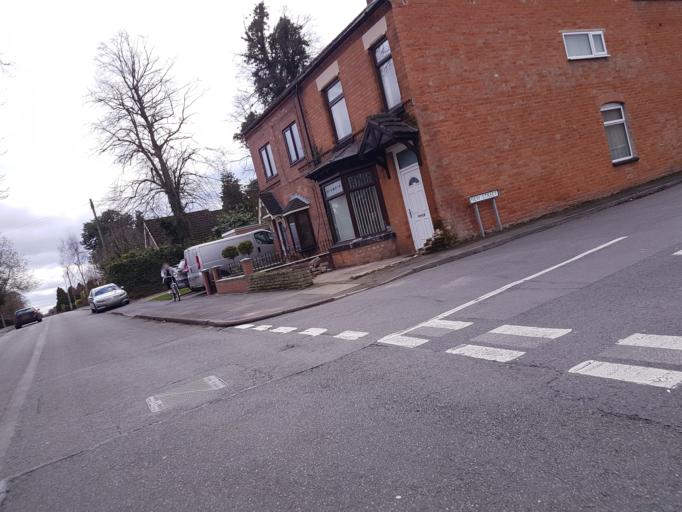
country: GB
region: England
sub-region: Leicestershire
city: Earl Shilton
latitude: 52.5709
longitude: -1.3175
